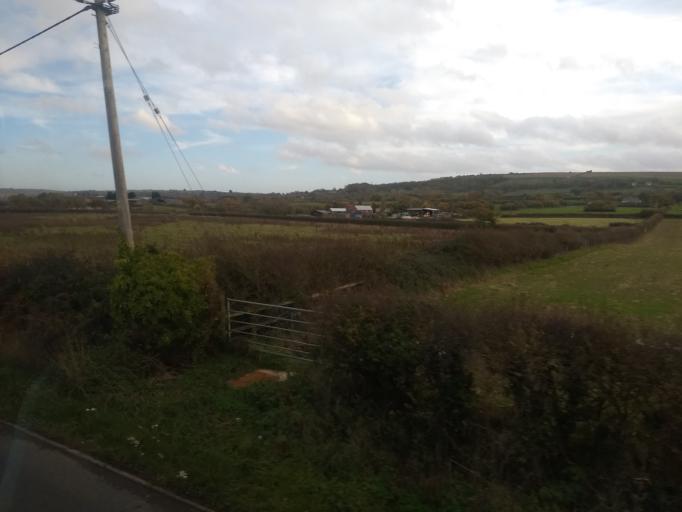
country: GB
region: England
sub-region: Isle of Wight
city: Northwood
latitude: 50.7033
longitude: -1.3405
